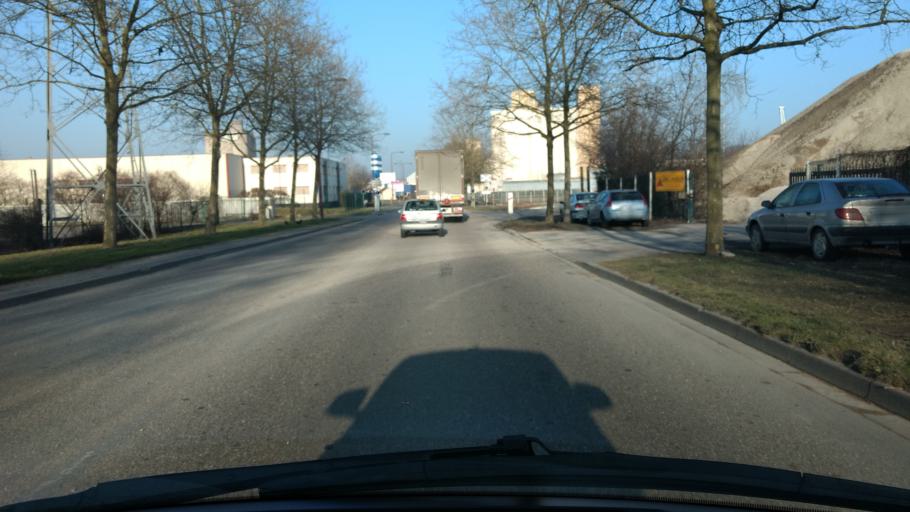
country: FR
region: Lorraine
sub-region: Departement de la Moselle
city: Metz
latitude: 49.1357
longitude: 6.1789
